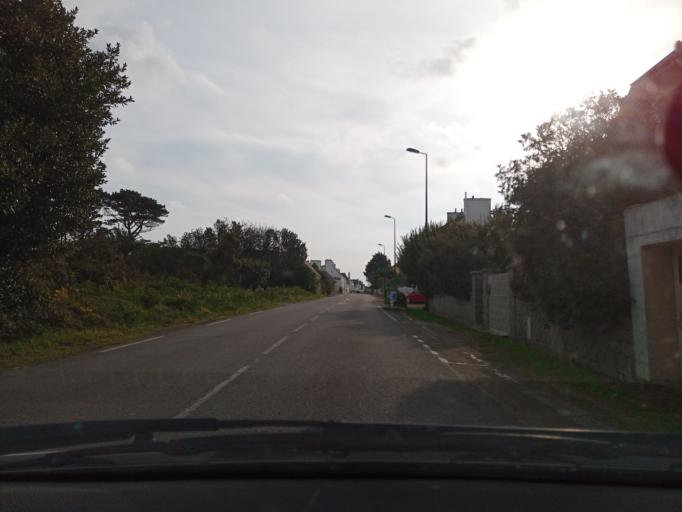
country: FR
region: Brittany
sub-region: Departement du Finistere
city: Plozevet
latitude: 47.9915
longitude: -4.4208
